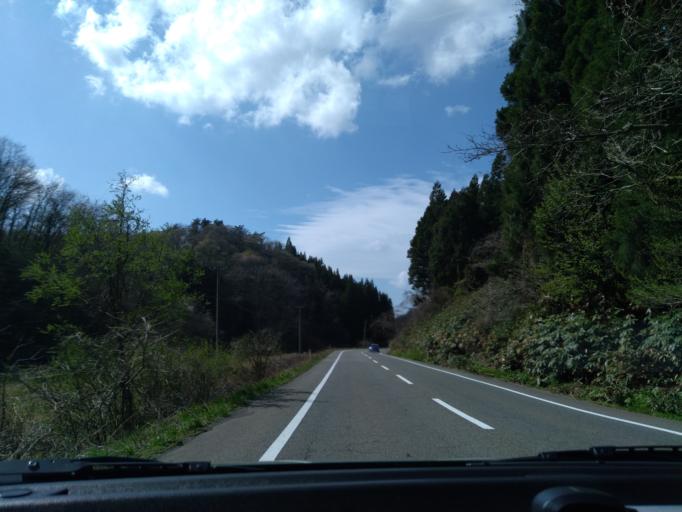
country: JP
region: Akita
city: Akita
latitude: 39.7004
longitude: 140.2182
